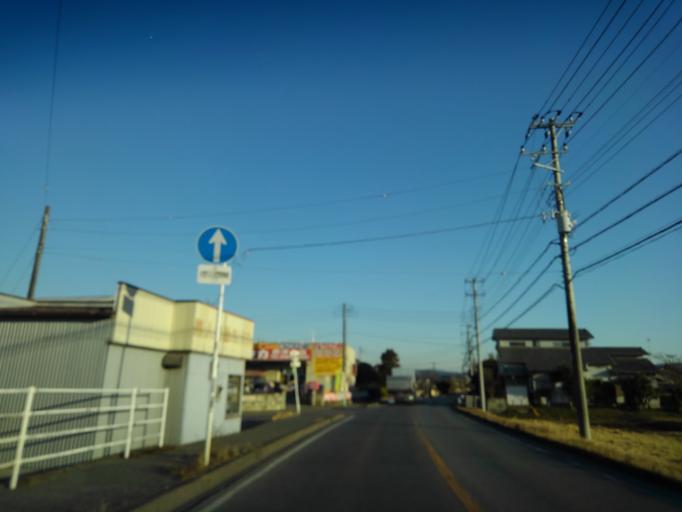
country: JP
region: Chiba
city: Kimitsu
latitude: 35.3180
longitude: 139.9291
